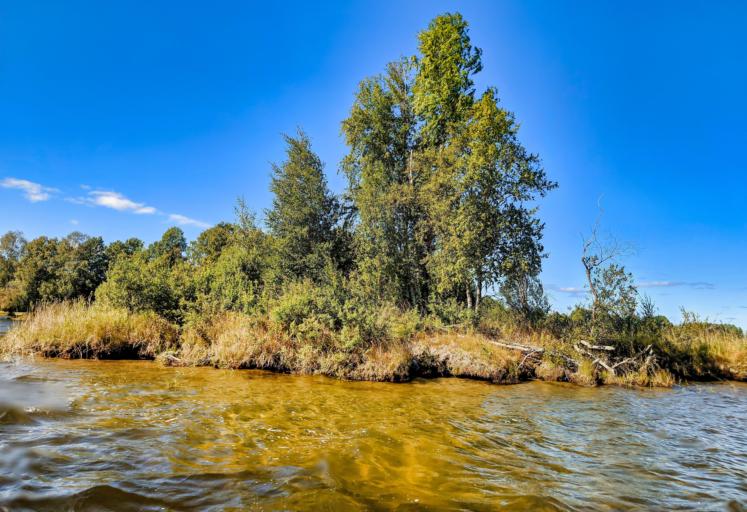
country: NO
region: Akershus
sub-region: Nannestad
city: Maura
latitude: 60.2830
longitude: 11.0918
